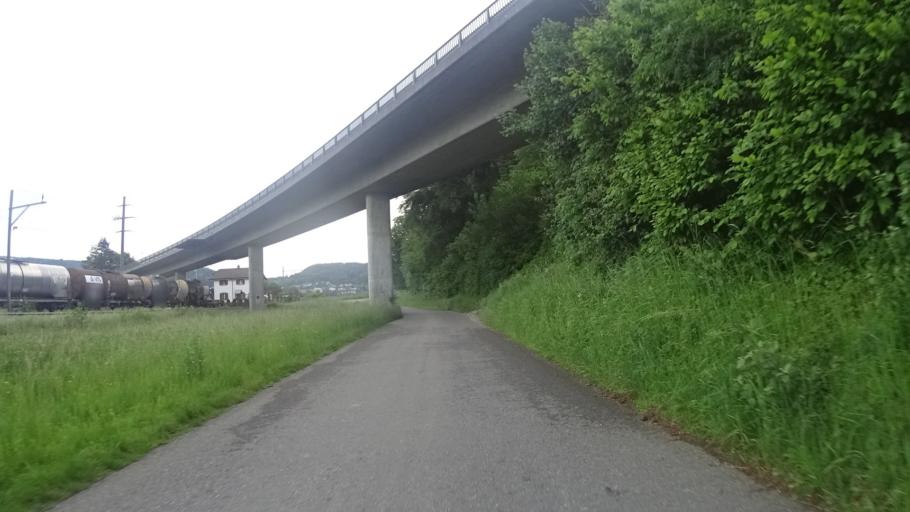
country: DE
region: Baden-Wuerttemberg
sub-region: Freiburg Region
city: Waldshut-Tiengen
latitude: 47.6114
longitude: 8.2015
